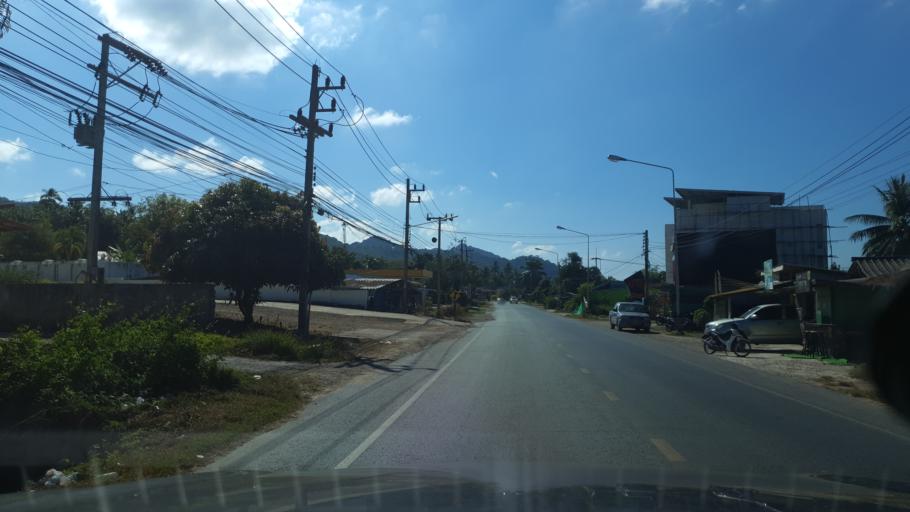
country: TH
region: Phangnga
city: Ban Ao Nang
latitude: 8.0603
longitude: 98.8136
